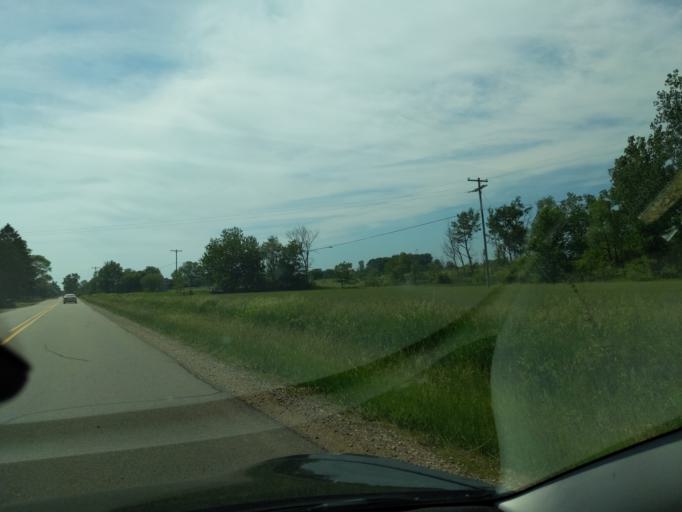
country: US
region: Michigan
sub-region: Eaton County
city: Grand Ledge
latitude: 42.7119
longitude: -84.7676
